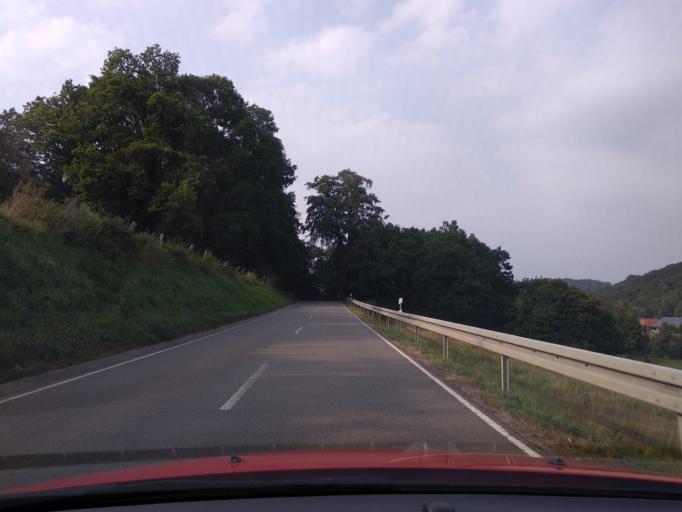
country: DE
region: Hesse
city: Liebenau
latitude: 51.4762
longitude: 9.2982
